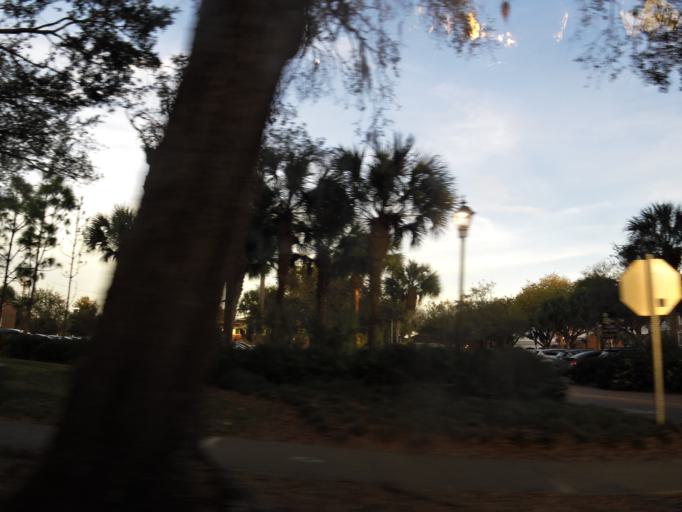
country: US
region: Florida
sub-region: Volusia County
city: DeLand
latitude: 29.0373
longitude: -81.3036
